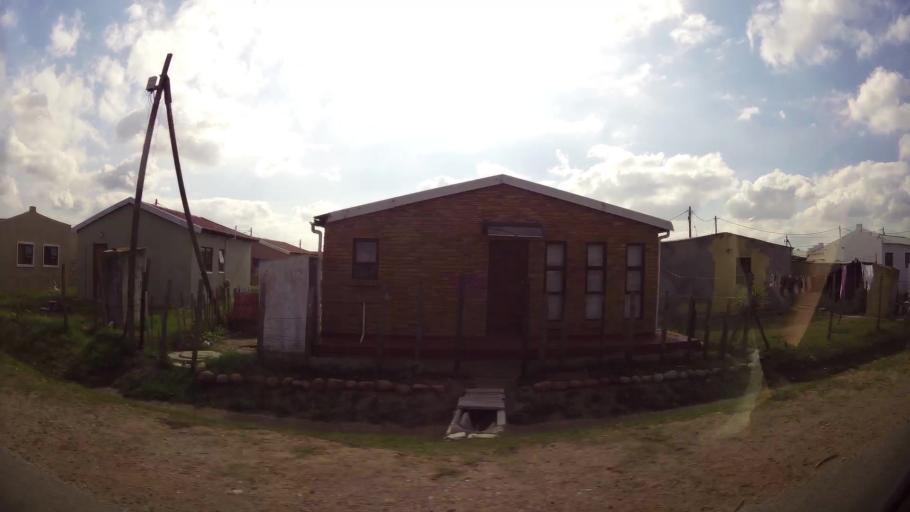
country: ZA
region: Eastern Cape
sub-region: Nelson Mandela Bay Metropolitan Municipality
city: Port Elizabeth
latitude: -33.7861
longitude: 25.5906
